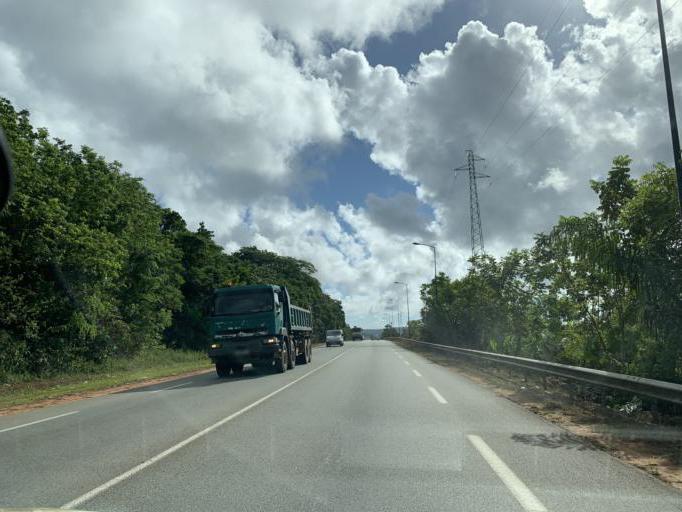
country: GF
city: Macouria
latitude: 4.8917
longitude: -52.3448
